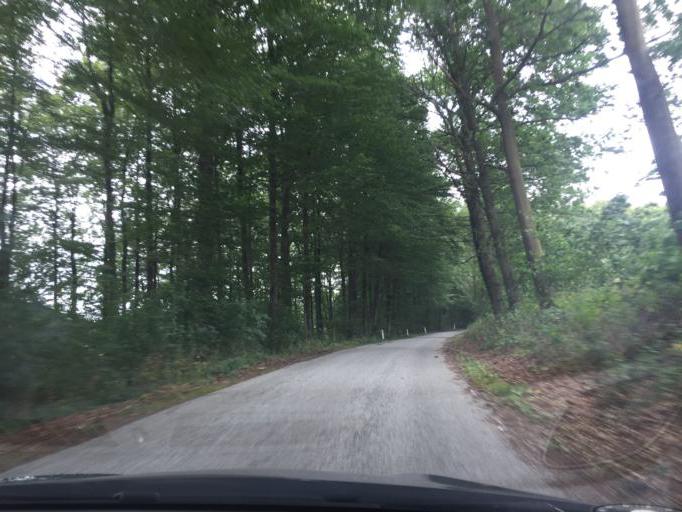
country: DK
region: South Denmark
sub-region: Assens Kommune
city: Arup
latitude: 55.3836
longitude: 10.0422
